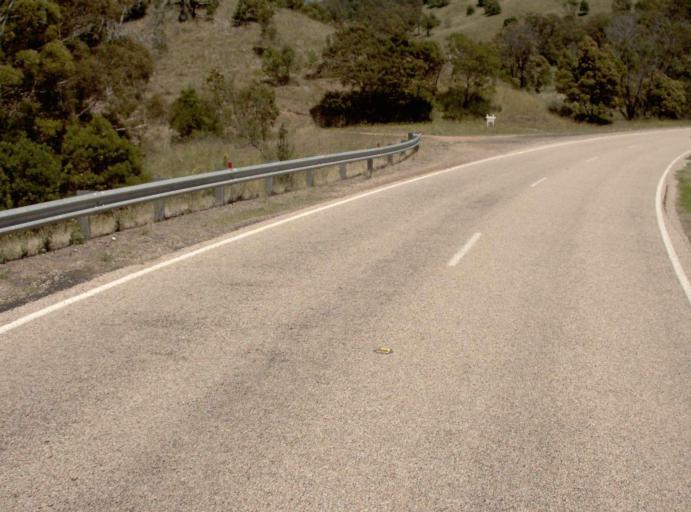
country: AU
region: Victoria
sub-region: Alpine
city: Mount Beauty
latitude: -37.1655
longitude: 147.6594
